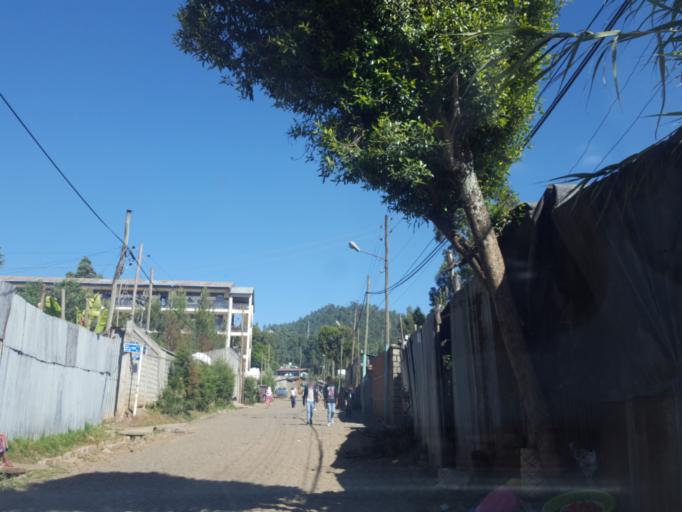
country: ET
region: Adis Abeba
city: Addis Ababa
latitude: 9.0568
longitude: 38.7467
